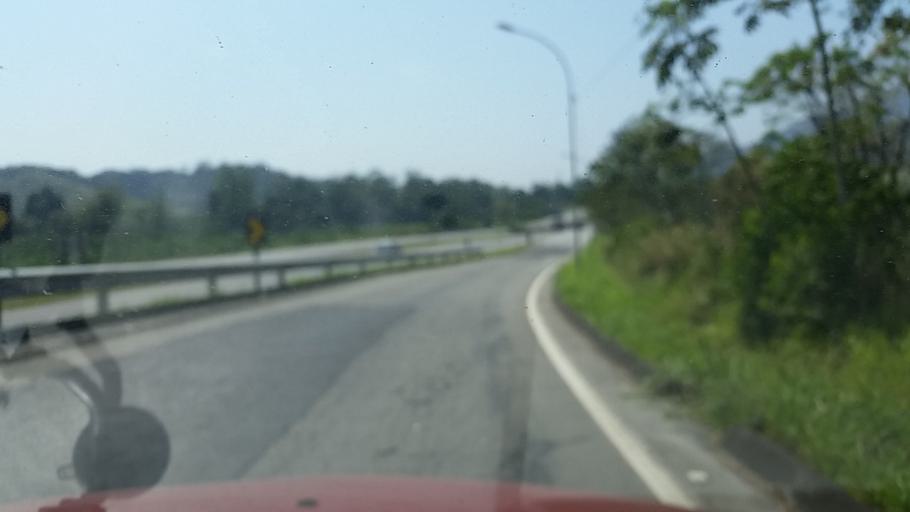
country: BR
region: Sao Paulo
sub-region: Miracatu
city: Miracatu
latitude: -24.3131
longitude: -47.5168
